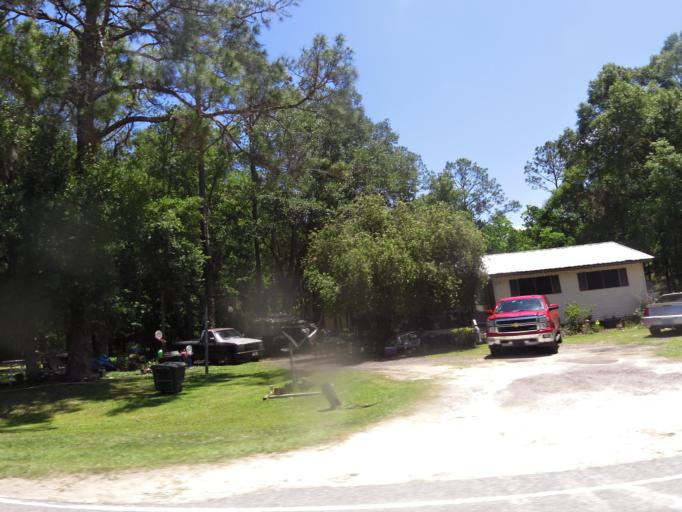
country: US
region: Florida
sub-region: Bradford County
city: Starke
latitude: 30.0387
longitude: -82.0684
